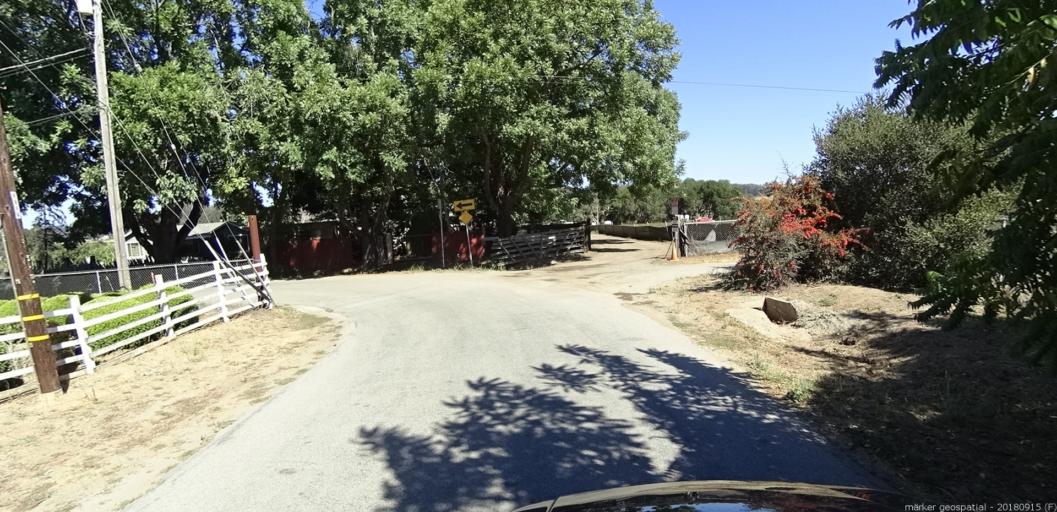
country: US
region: California
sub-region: Monterey County
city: Las Lomas
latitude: 36.8570
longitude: -121.7040
